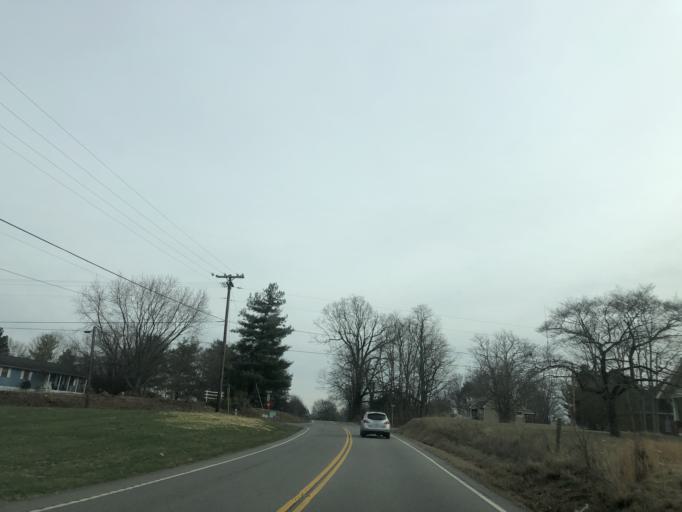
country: US
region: Tennessee
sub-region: Sumner County
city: White House
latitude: 36.4790
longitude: -86.5765
